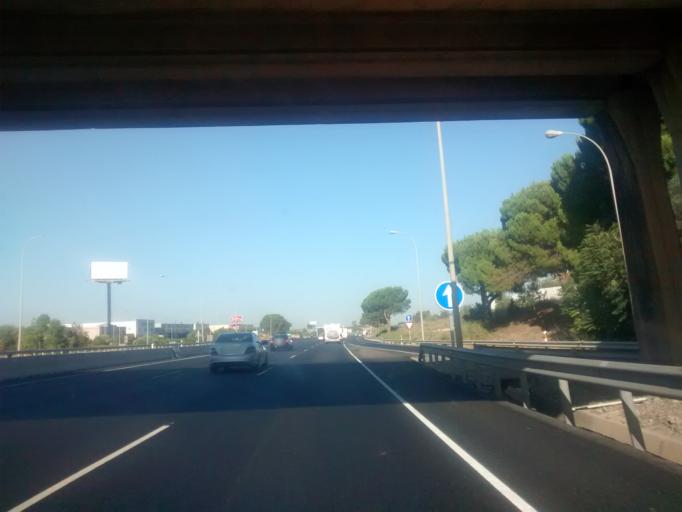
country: ES
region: Andalusia
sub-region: Provincia de Sevilla
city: Umbrete
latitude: 37.3601
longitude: -6.1416
